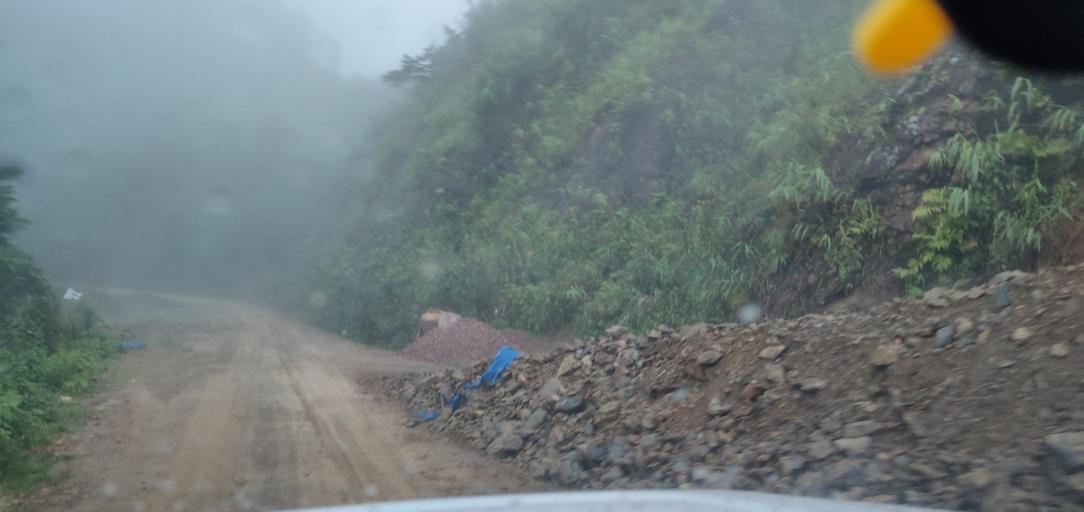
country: LA
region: Phongsali
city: Phongsali
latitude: 21.3988
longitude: 102.1899
